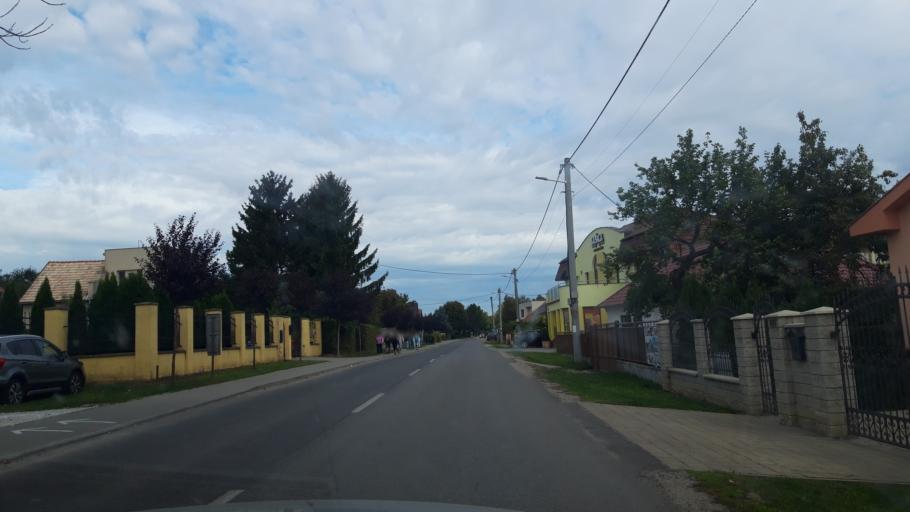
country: SK
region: Nitriansky
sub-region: Okres Nitra
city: Vrable
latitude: 48.1023
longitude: 18.3375
